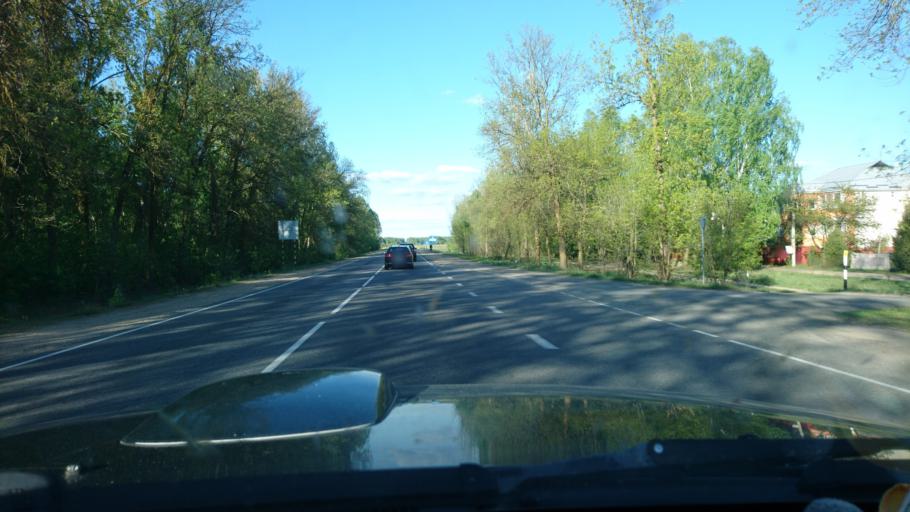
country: BY
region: Brest
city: Byaroza
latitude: 52.5481
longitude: 25.0124
